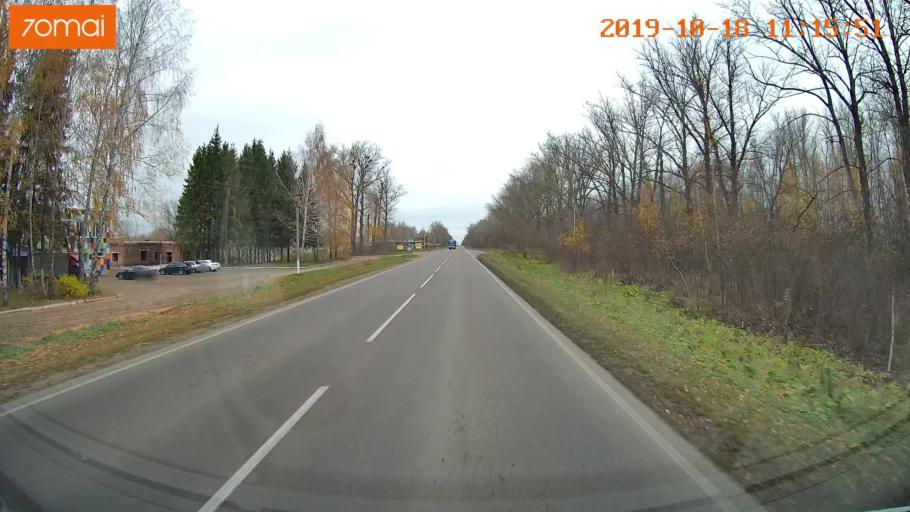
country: RU
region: Tula
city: Kimovsk
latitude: 53.9985
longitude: 38.5479
